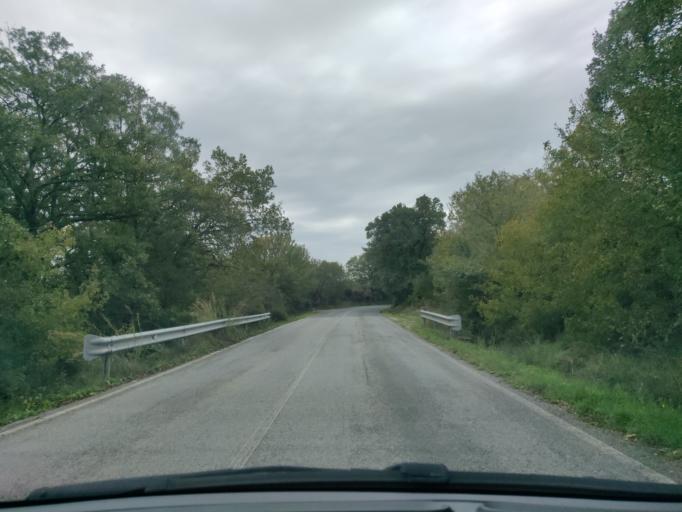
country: IT
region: Latium
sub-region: Citta metropolitana di Roma Capitale
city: Allumiere
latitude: 42.1335
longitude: 11.8696
